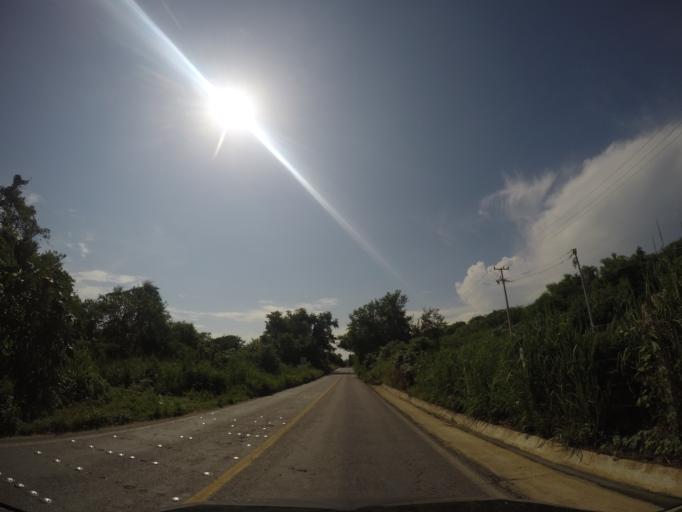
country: MX
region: Oaxaca
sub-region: San Pedro Mixtepec -Dto. 22 -
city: Puerto Escondido
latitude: 15.8868
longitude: -97.1130
